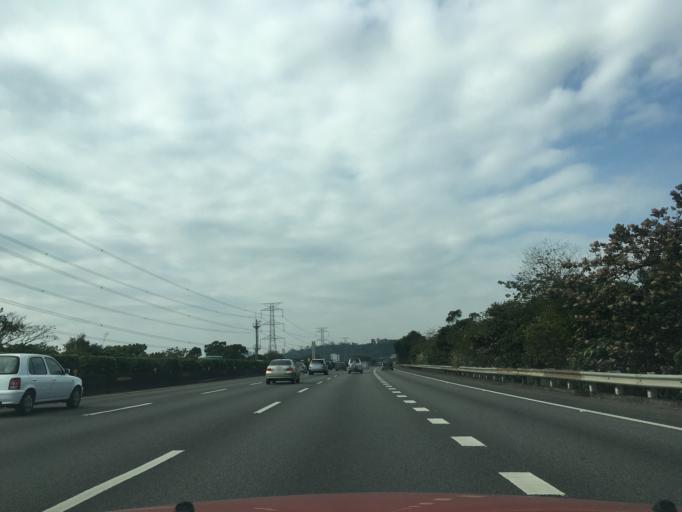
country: TW
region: Taiwan
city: Daxi
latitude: 24.9264
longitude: 121.3077
